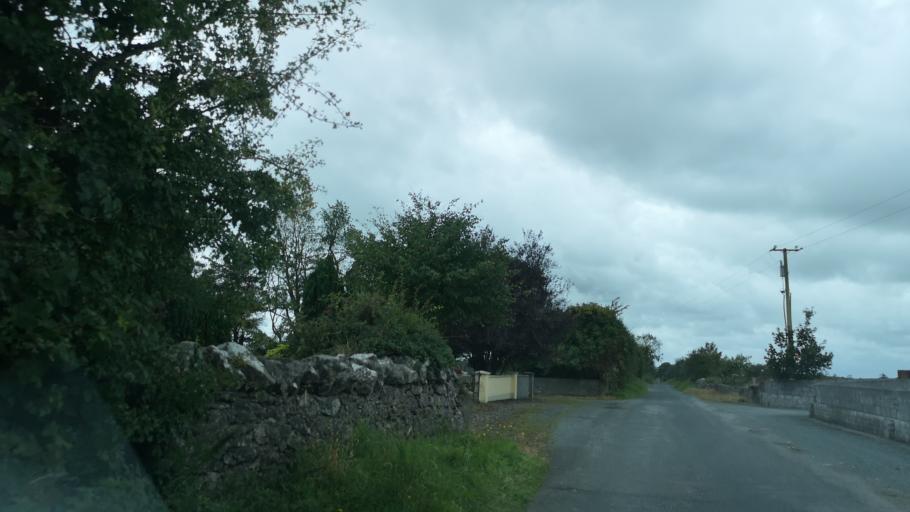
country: IE
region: Connaught
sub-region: County Galway
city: Athenry
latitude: 53.3242
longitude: -8.7475
